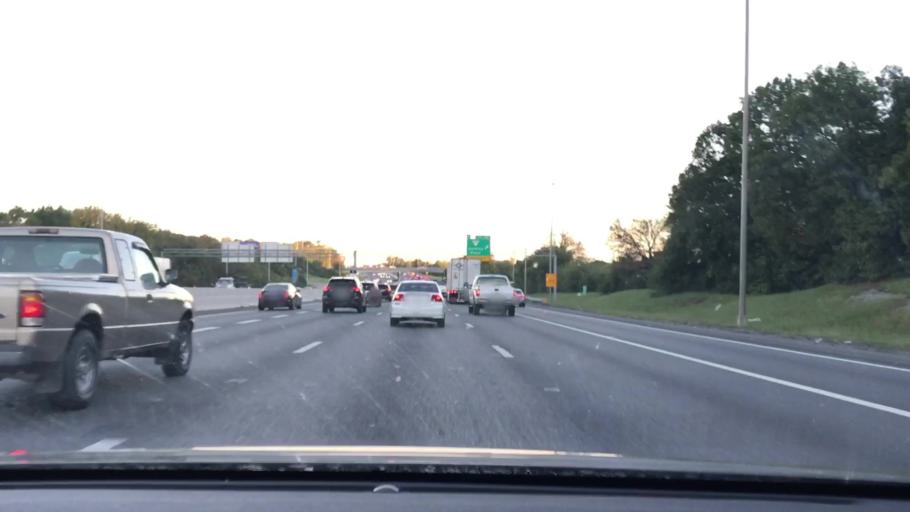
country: US
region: Tennessee
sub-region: Davidson County
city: Oak Hill
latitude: 36.0820
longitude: -86.6974
